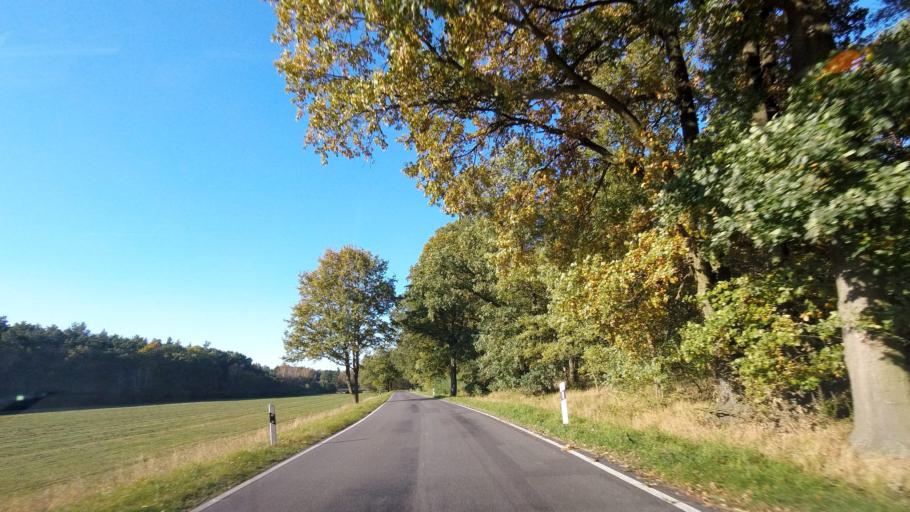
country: DE
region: Saxony-Anhalt
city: Kropstadt
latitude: 51.9688
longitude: 12.7864
